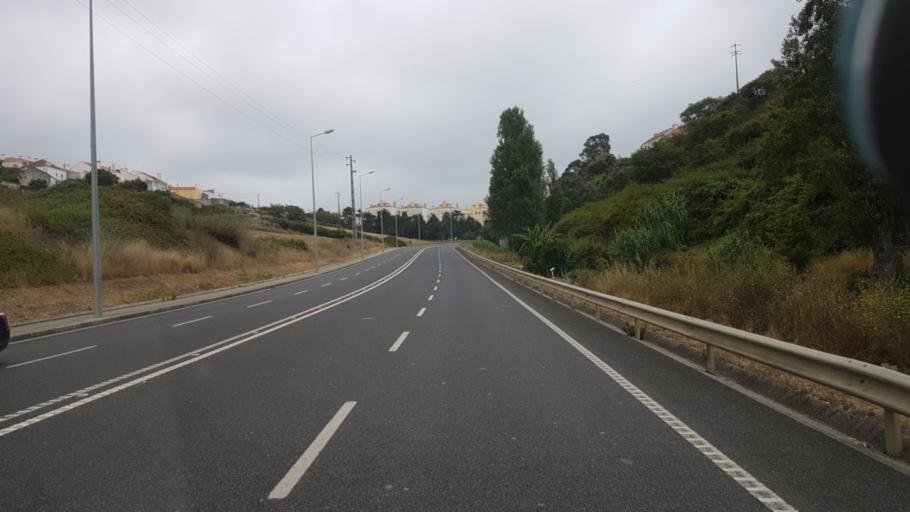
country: PT
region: Lisbon
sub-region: Mafra
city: Mafra
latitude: 38.9344
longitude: -9.3389
